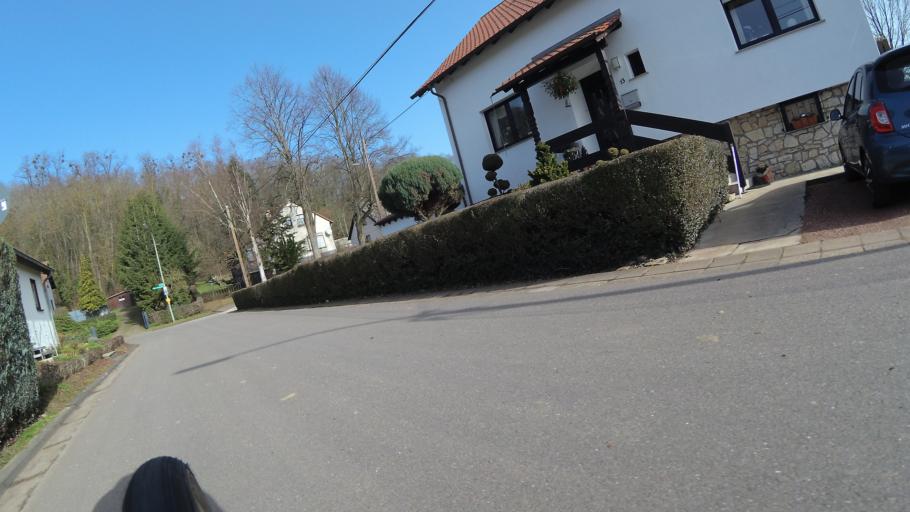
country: DE
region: Saarland
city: Uberherrn
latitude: 49.2765
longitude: 6.6988
